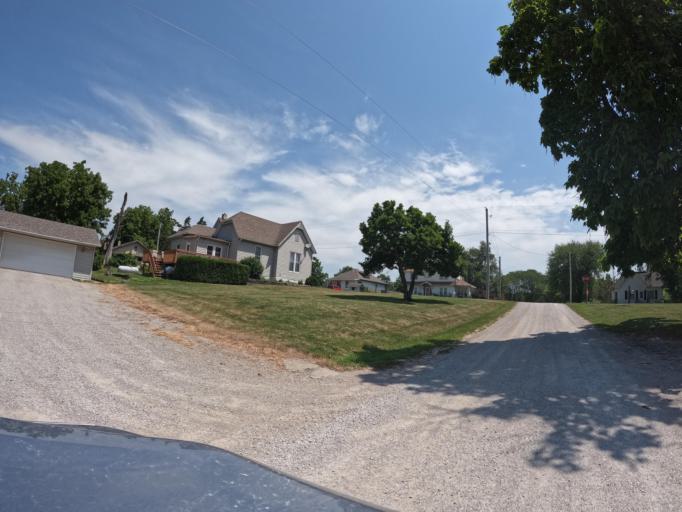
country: US
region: Iowa
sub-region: Appanoose County
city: Centerville
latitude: 40.7825
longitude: -92.9459
